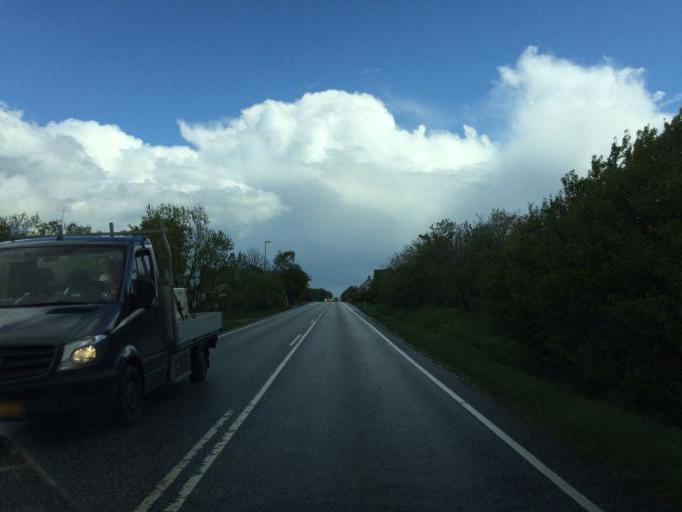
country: DK
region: Central Jutland
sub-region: Holstebro Kommune
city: Holstebro
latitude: 56.4003
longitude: 8.6741
